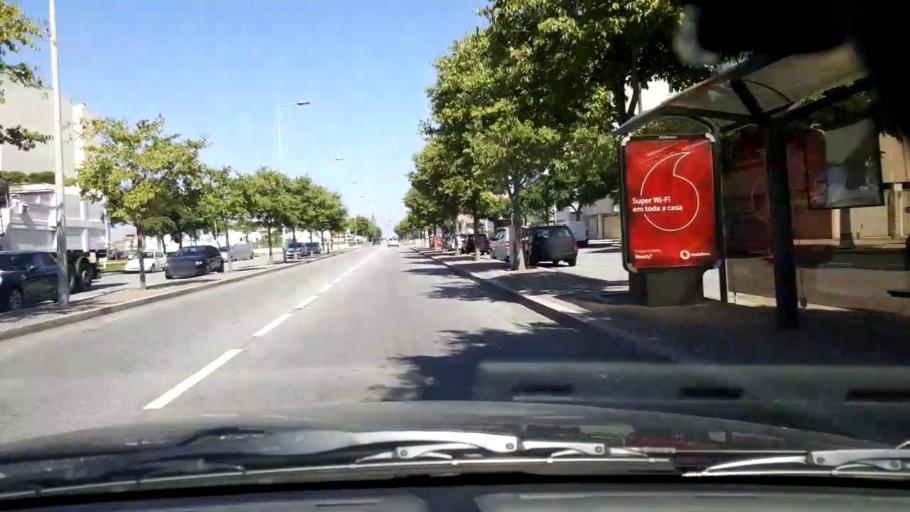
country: PT
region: Porto
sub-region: Vila do Conde
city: Vila do Conde
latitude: 41.3621
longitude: -8.7460
